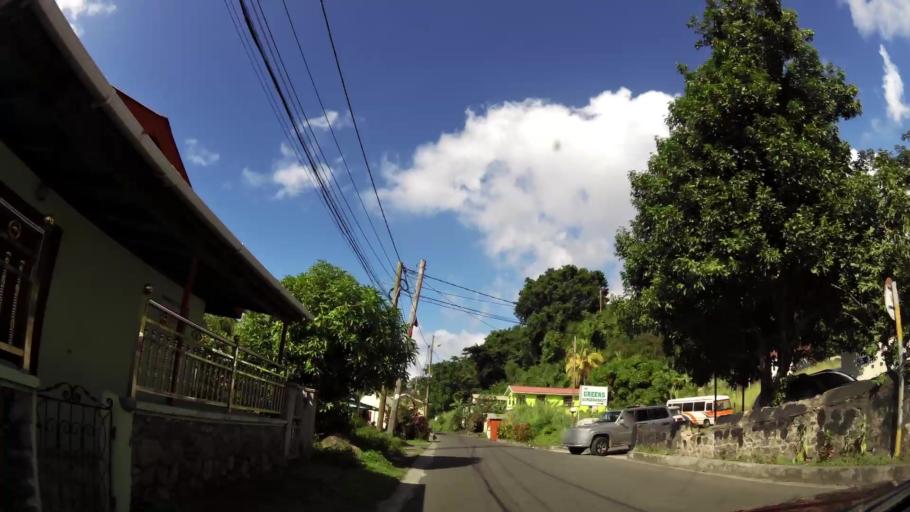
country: DM
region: Saint Luke
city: Pointe Michel
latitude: 15.2783
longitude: -61.3743
